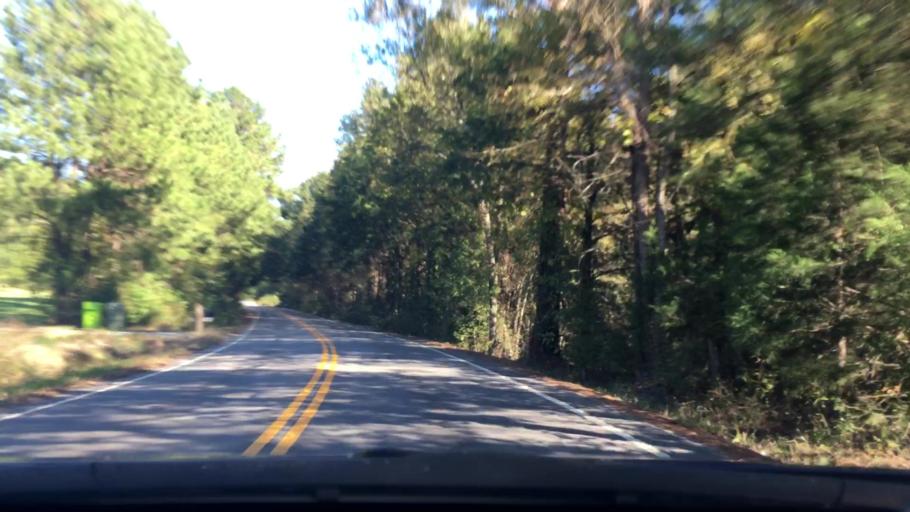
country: US
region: South Carolina
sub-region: Lexington County
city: Irmo
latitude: 34.1112
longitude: -81.1701
